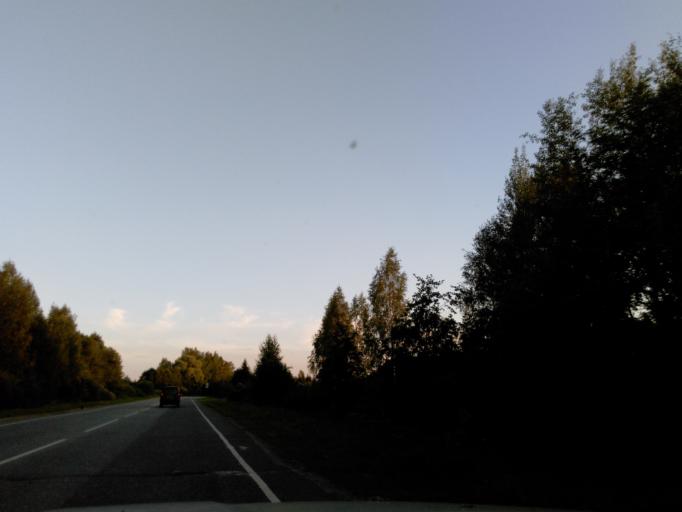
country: RU
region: Tverskaya
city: Konakovo
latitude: 56.6448
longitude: 36.7089
